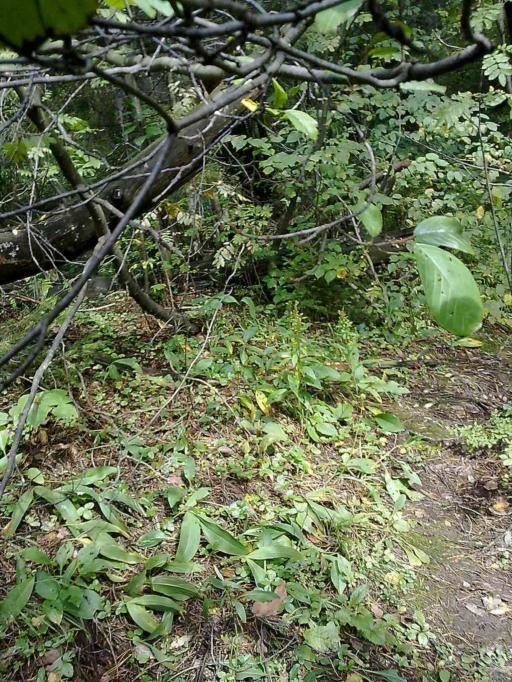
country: RU
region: Moskovskaya
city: Gorki Vtoryye
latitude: 55.6814
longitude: 37.1564
